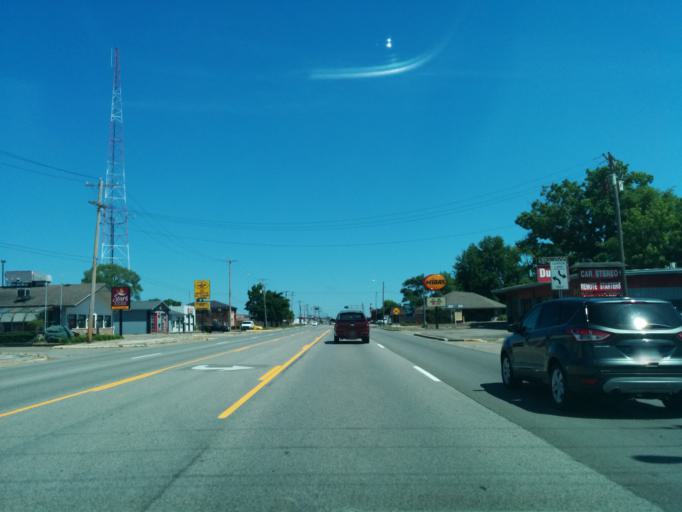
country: US
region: Michigan
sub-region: Bay County
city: Bay City
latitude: 43.6038
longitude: -83.9151
